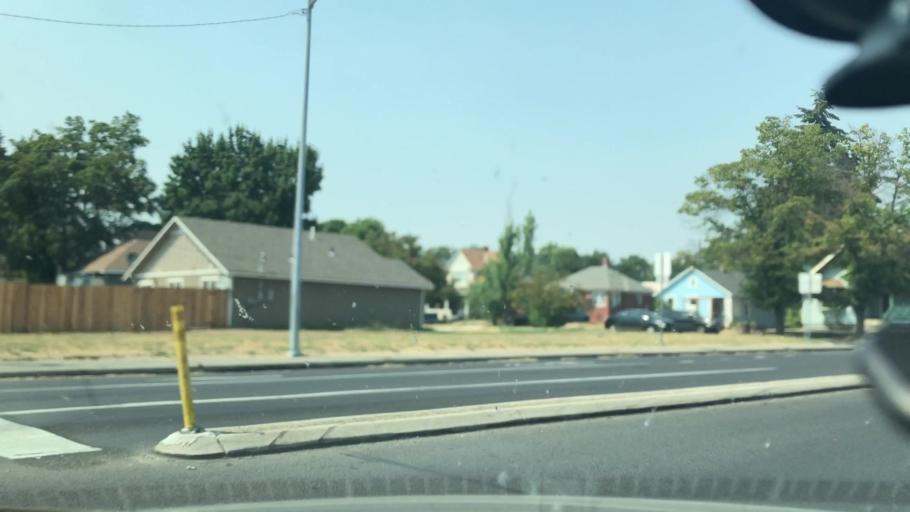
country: US
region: Washington
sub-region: Spokane County
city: Spokane
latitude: 47.6863
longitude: -117.3790
